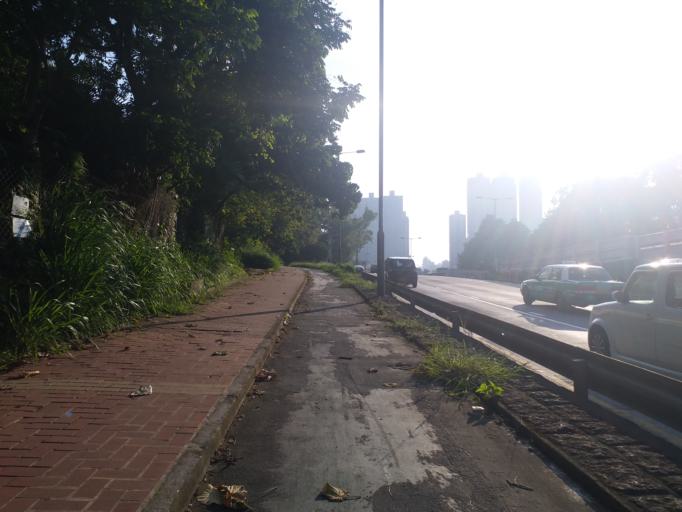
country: HK
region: Yuen Long
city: Yuen Long Kau Hui
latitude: 22.4440
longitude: 114.0471
